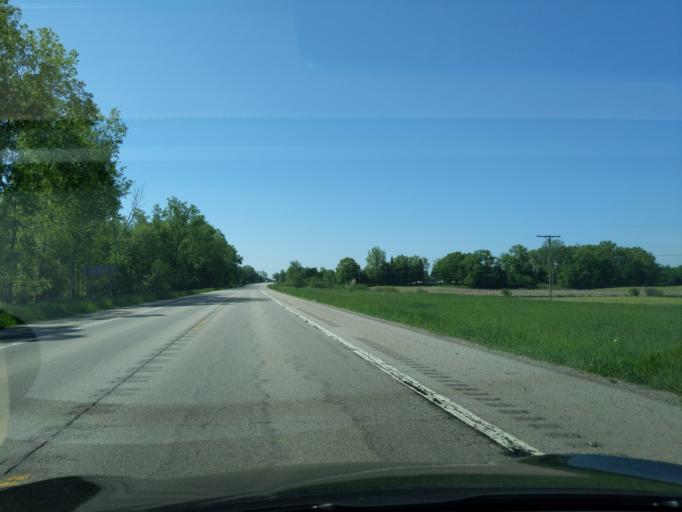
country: US
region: Michigan
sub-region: Ingham County
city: Stockbridge
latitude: 42.5170
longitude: -84.1901
